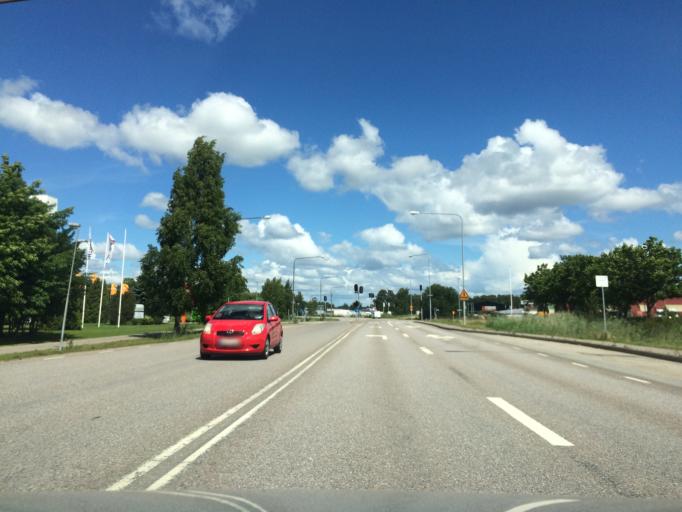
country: SE
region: Vaestra Goetaland
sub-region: Trollhattan
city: Trollhattan
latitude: 58.2972
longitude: 12.3216
